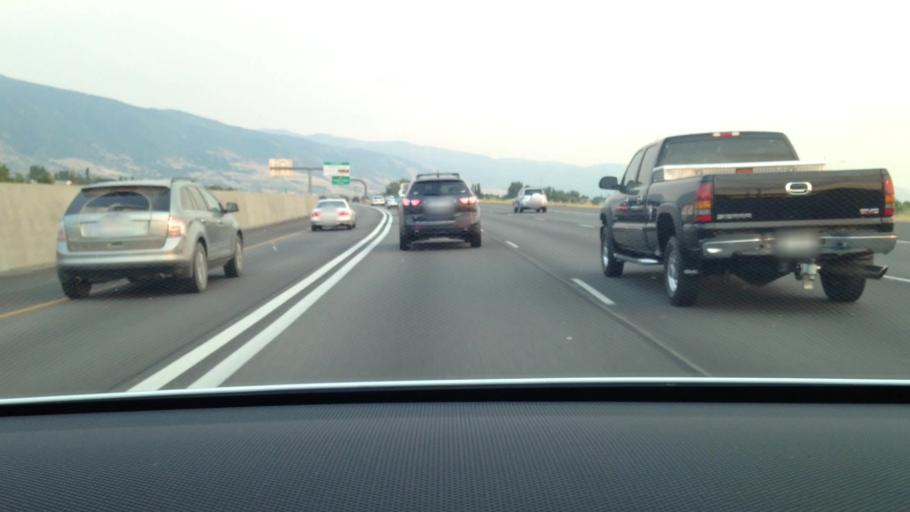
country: US
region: Utah
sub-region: Davis County
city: Kaysville
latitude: 41.0102
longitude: -111.9390
